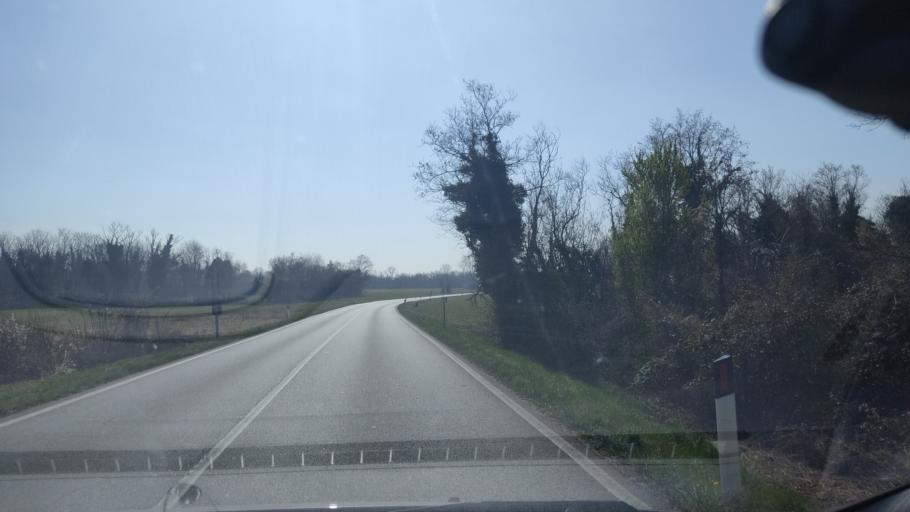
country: IT
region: Friuli Venezia Giulia
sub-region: Provincia di Pordenone
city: Budoia
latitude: 46.0346
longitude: 12.5495
